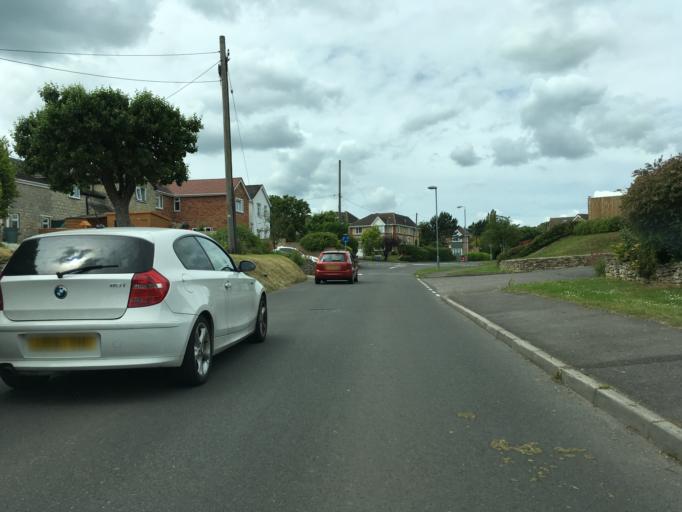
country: GB
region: England
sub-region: Wiltshire
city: Purton
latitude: 51.5698
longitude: -1.8610
